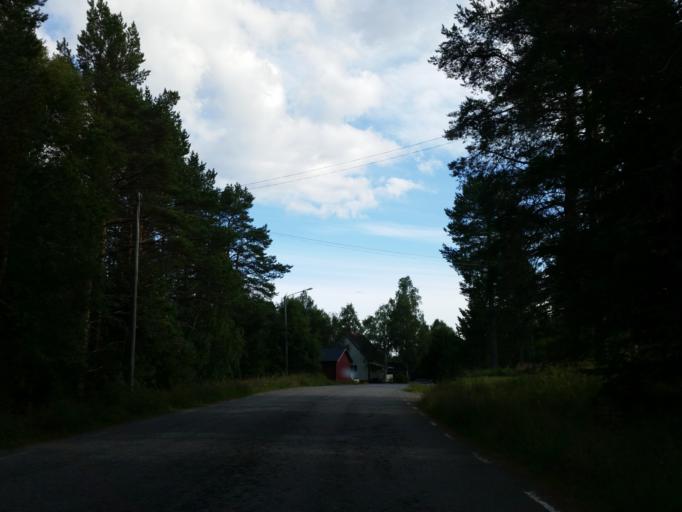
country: SE
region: Vaesterbotten
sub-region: Robertsfors Kommun
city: Robertsfors
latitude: 64.0539
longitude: 20.8544
